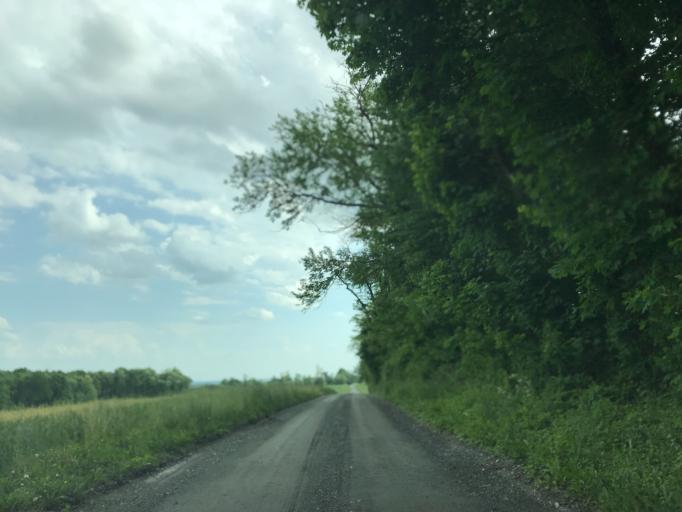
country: US
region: Pennsylvania
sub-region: York County
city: Susquehanna Trails
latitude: 39.7042
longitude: -76.3410
